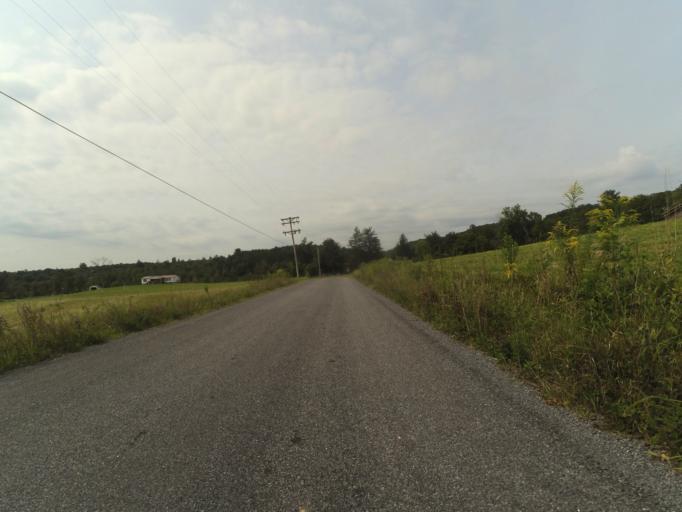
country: US
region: Pennsylvania
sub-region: Huntingdon County
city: Huntingdon
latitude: 40.5964
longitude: -78.0586
